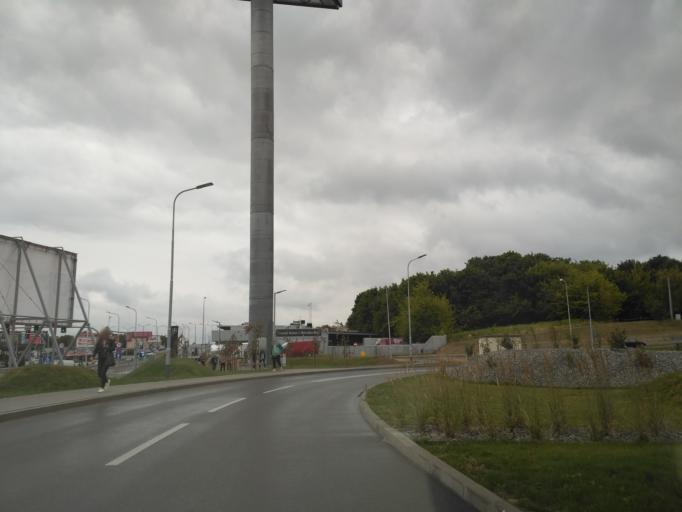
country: PL
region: Lublin Voivodeship
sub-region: Powiat lubelski
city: Lublin
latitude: 51.2813
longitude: 22.5745
